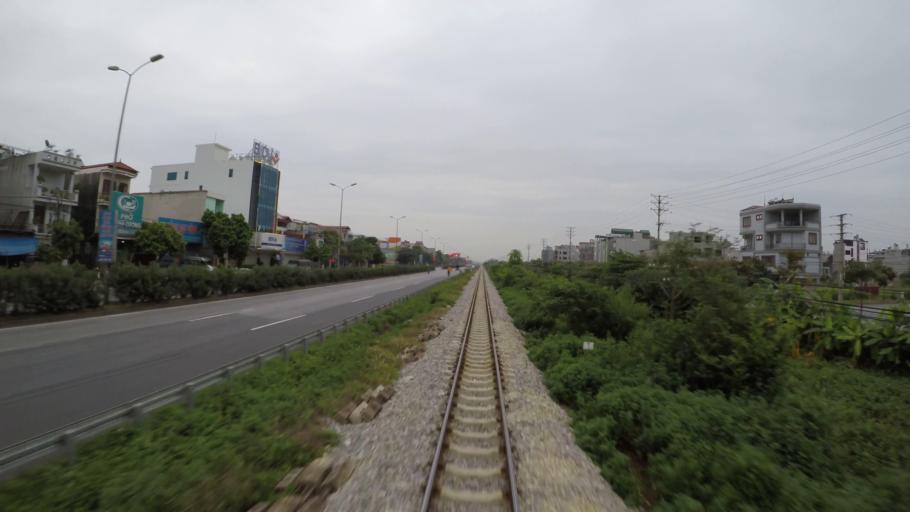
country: VN
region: Hung Yen
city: Nhu Quynh
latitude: 20.9828
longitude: 105.9799
